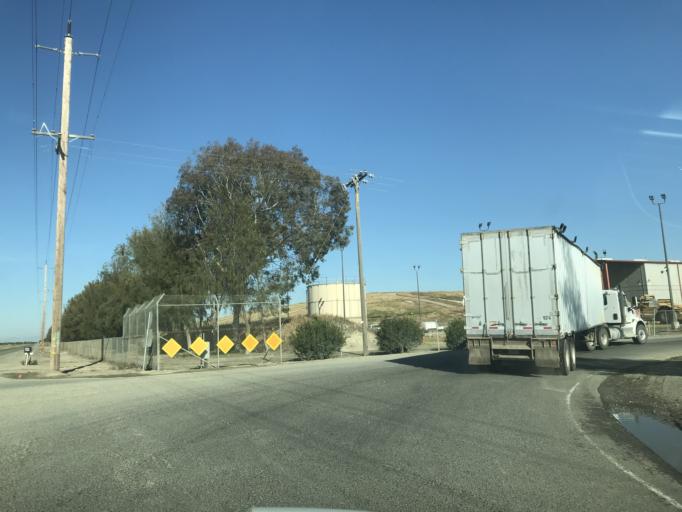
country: US
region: California
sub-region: Fresno County
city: San Joaquin
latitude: 36.6618
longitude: -120.1332
